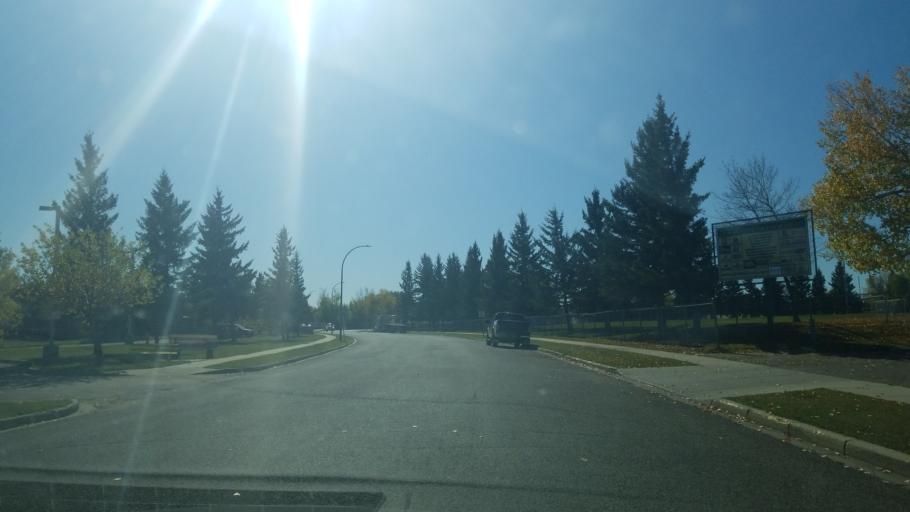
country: CA
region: Saskatchewan
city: Lloydminster
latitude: 53.2748
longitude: -110.0198
